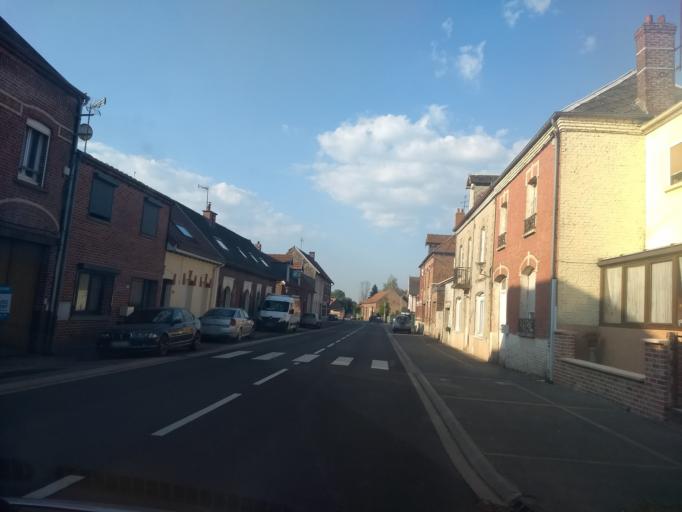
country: FR
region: Nord-Pas-de-Calais
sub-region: Departement du Pas-de-Calais
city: Bucquoy
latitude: 50.1377
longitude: 2.7088
